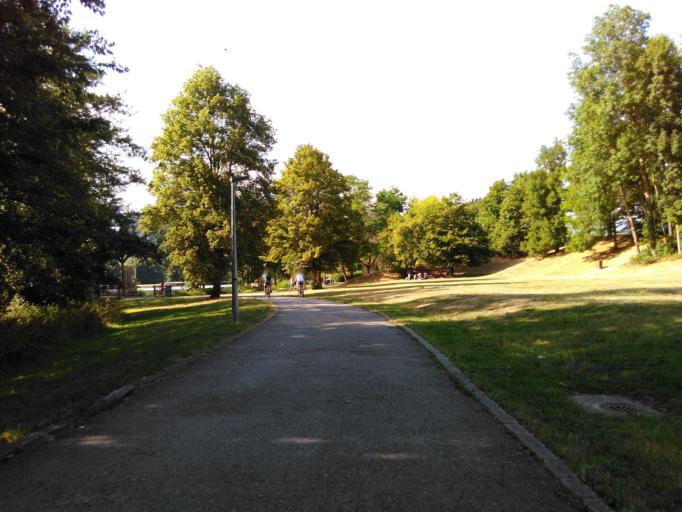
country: LU
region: Grevenmacher
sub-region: Canton d'Echternach
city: Echternach
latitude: 49.7993
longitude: 6.4164
